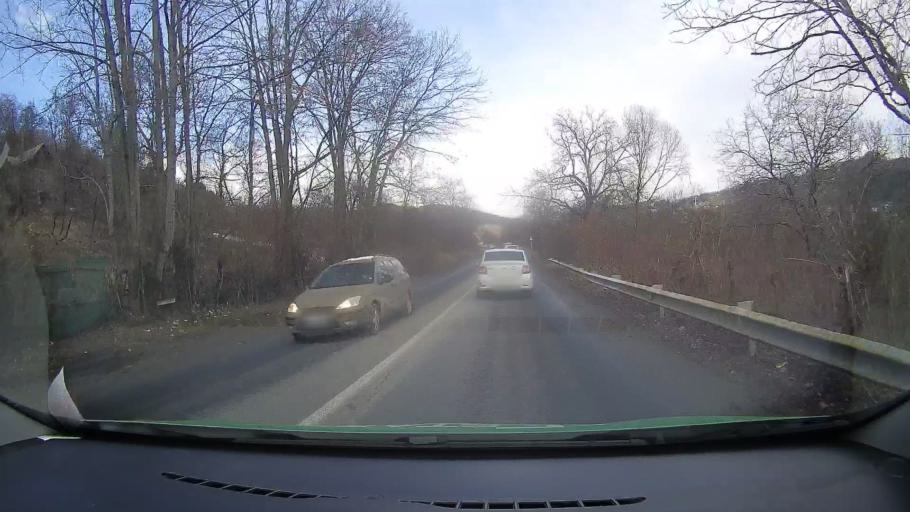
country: RO
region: Dambovita
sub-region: Comuna Pietrosita
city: Pietrosita
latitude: 45.1782
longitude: 25.4409
